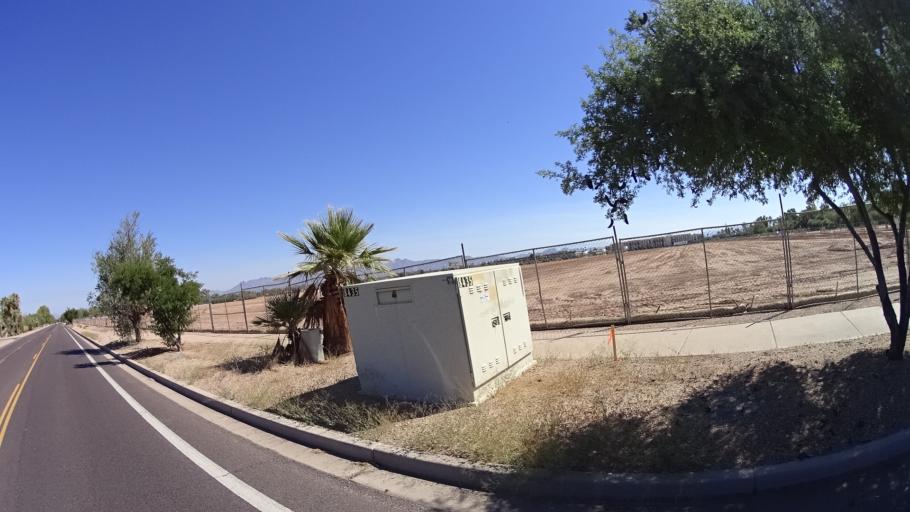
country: US
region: Arizona
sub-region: Maricopa County
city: Paradise Valley
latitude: 33.5318
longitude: -111.9344
